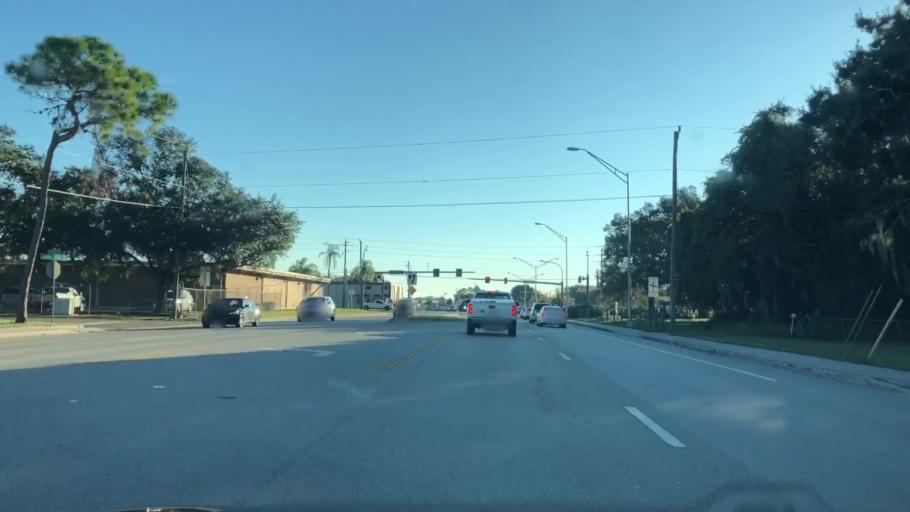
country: US
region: Florida
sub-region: Sarasota County
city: Fruitville
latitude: 27.3230
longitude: -82.4528
